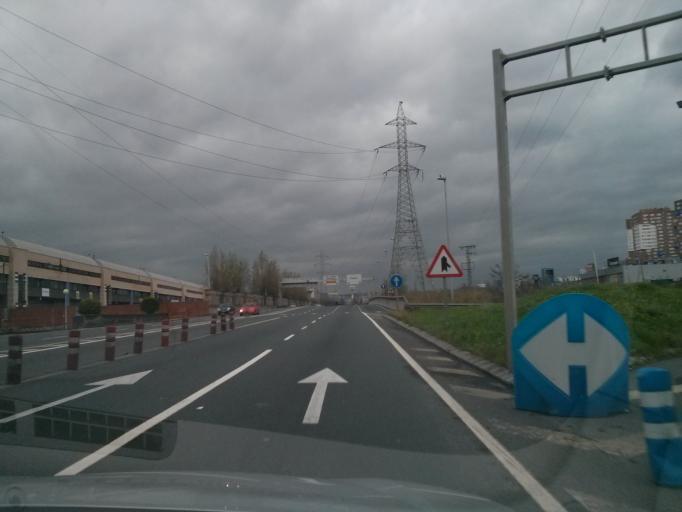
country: ES
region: Basque Country
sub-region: Bizkaia
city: Barakaldo
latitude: 43.2915
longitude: -3.0097
